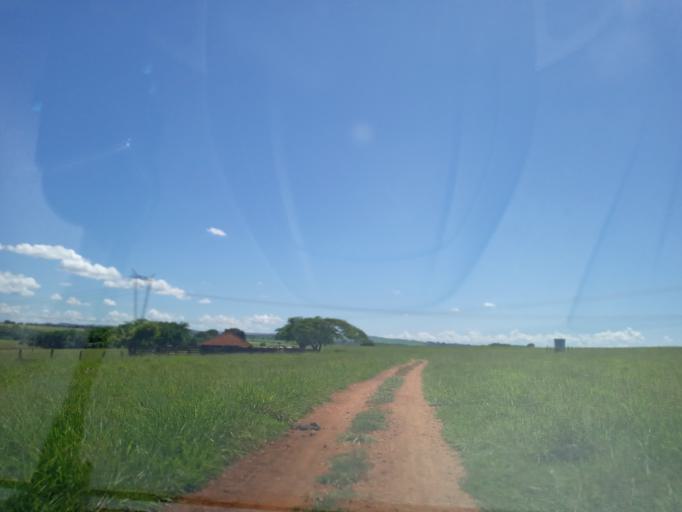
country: BR
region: Goias
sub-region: Itumbiara
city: Itumbiara
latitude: -18.3979
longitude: -49.1253
